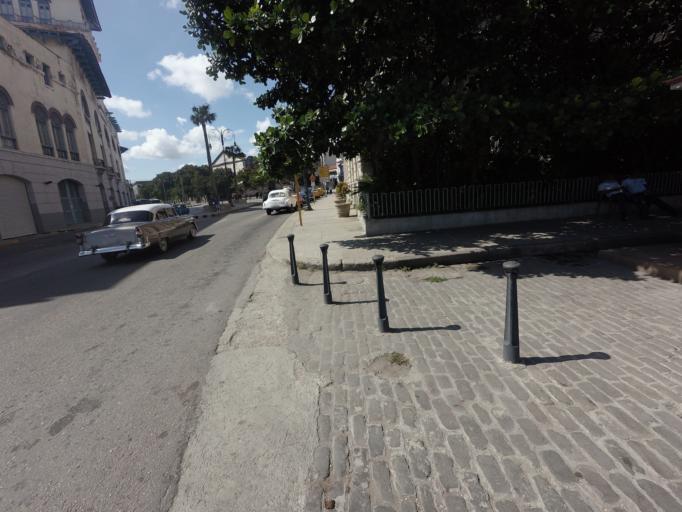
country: TM
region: Balkan
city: Gumdag
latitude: 38.8429
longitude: 54.1892
